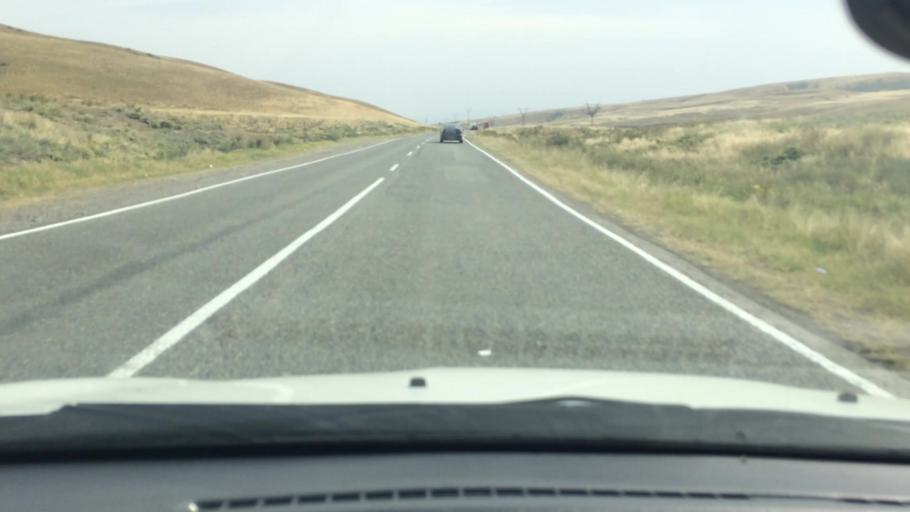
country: GE
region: Kvemo Kartli
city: Rust'avi
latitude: 41.5053
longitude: 44.9534
